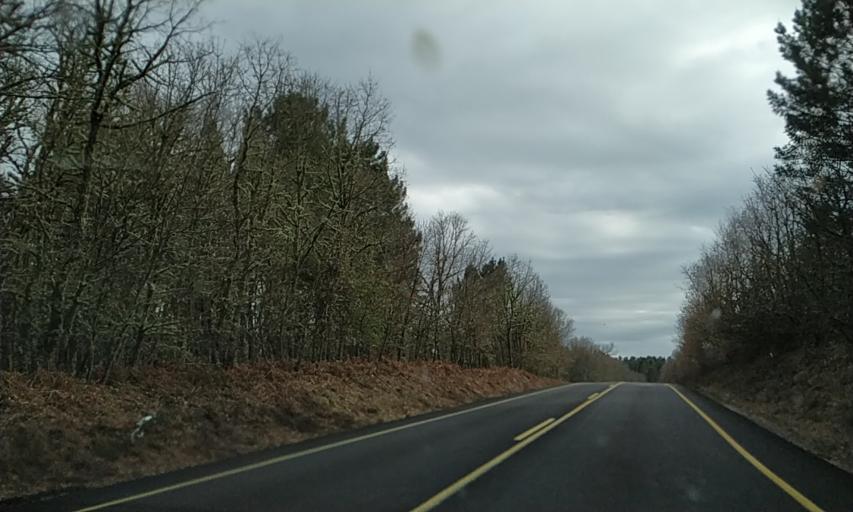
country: ES
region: Castille and Leon
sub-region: Provincia de Salamanca
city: Penaparda
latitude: 40.3065
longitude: -6.6509
